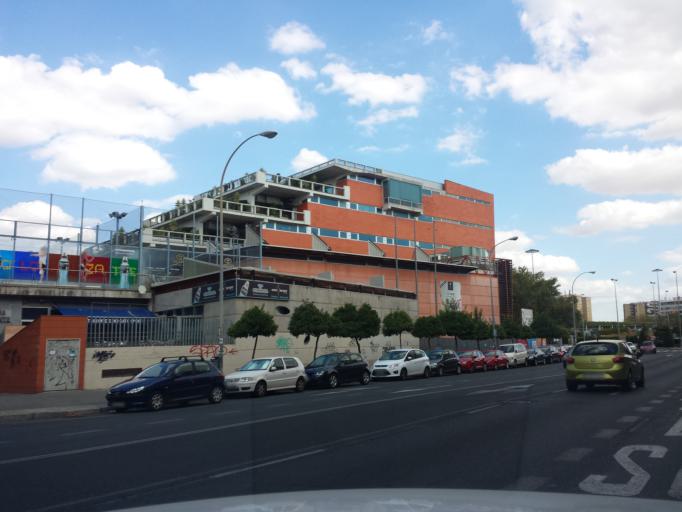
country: ES
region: Andalusia
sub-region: Provincia de Sevilla
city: Sevilla
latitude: 37.3923
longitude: -5.9795
